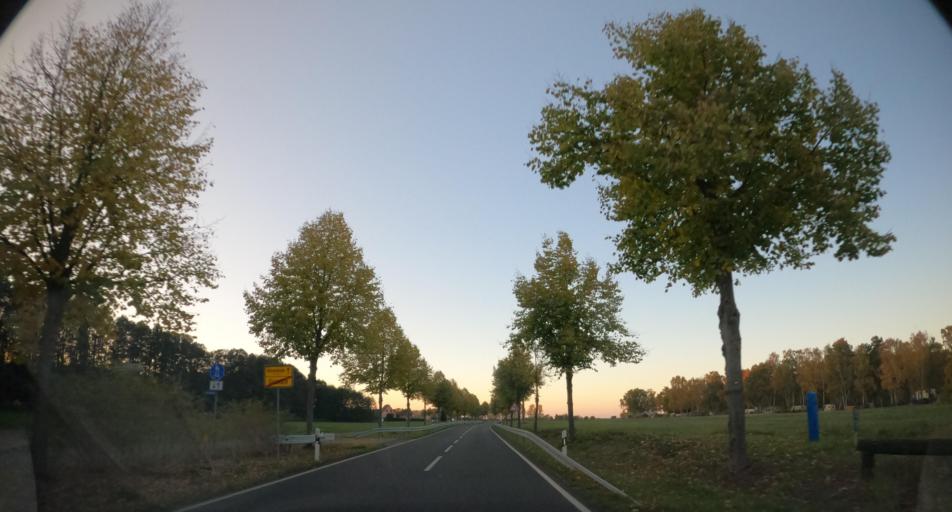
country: DE
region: Mecklenburg-Vorpommern
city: Ueckermunde
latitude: 53.7601
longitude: 14.0093
